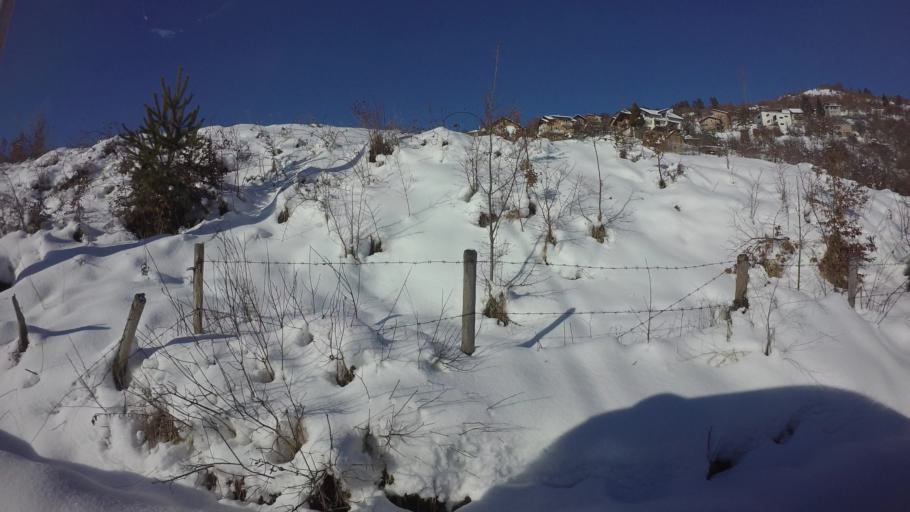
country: BA
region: Federation of Bosnia and Herzegovina
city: Kobilja Glava
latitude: 43.8948
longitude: 18.4097
